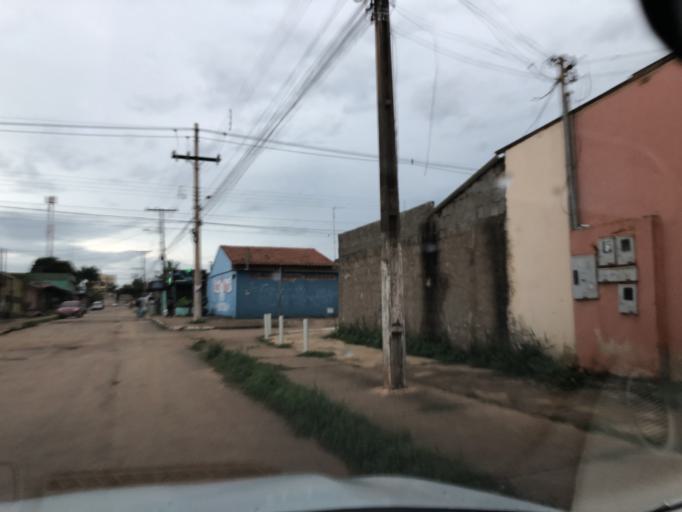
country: BR
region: Goias
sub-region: Luziania
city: Luziania
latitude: -16.1108
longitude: -47.9726
